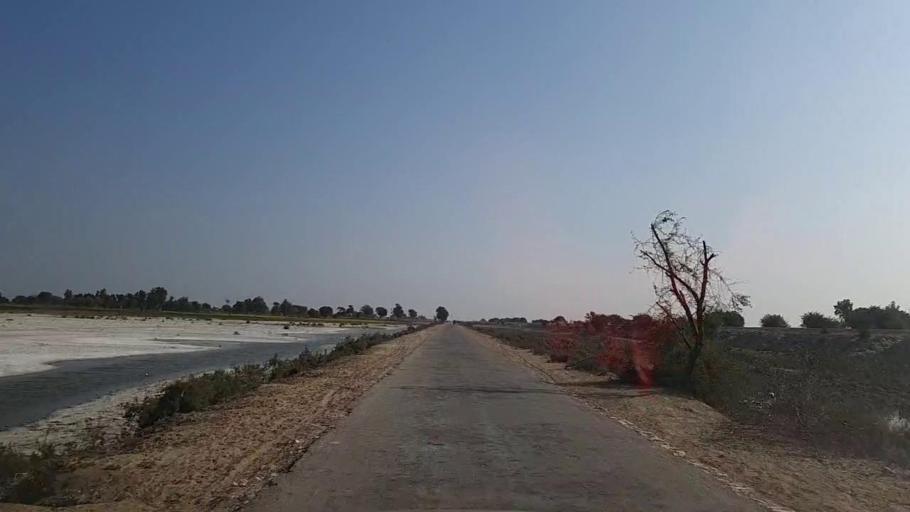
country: PK
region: Sindh
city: Sanghar
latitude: 25.9740
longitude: 69.0289
